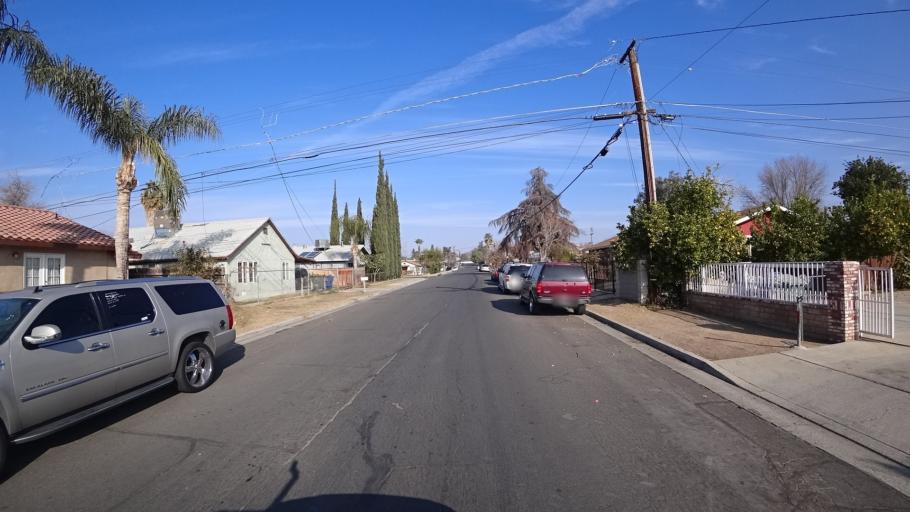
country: US
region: California
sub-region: Kern County
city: Bakersfield
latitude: 35.3942
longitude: -118.9807
